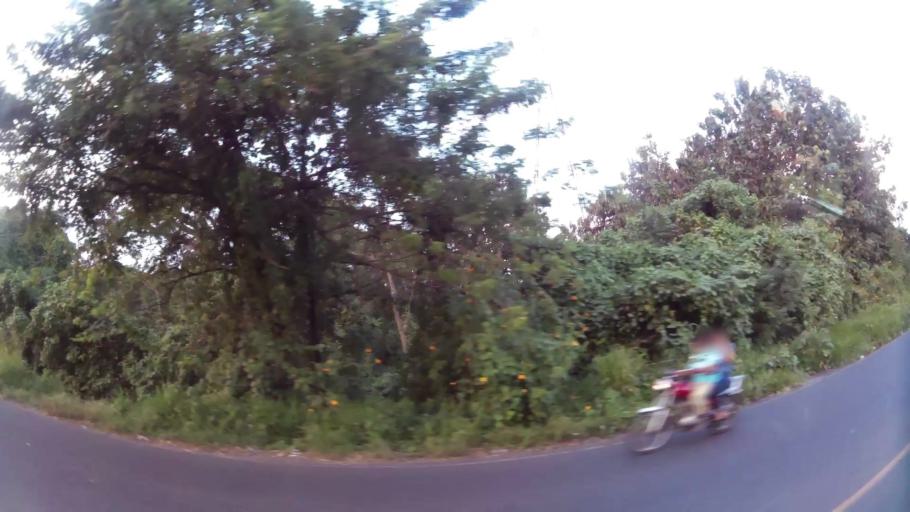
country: GT
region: Retalhuleu
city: Santa Cruz Mulua
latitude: 14.5744
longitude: -91.6308
